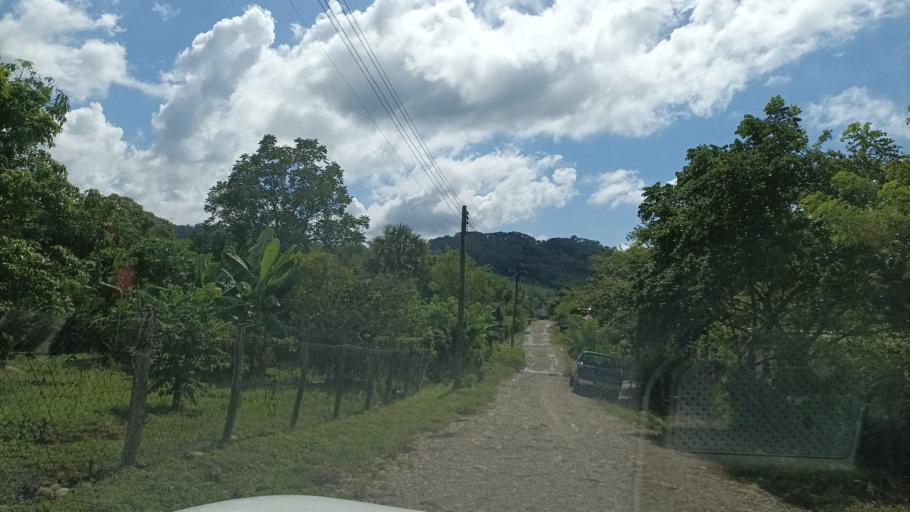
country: MX
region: Veracruz
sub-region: Tantoyuca
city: El Lindero
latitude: 21.1960
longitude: -98.1443
